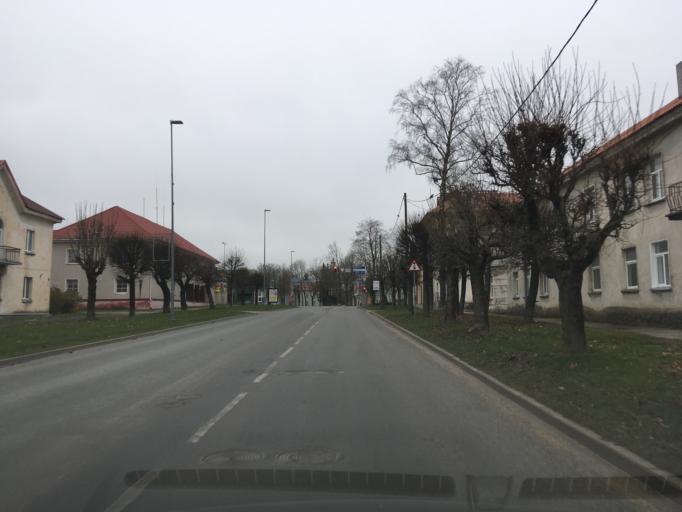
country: EE
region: Ida-Virumaa
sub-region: Johvi vald
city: Johvi
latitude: 59.3612
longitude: 27.4072
